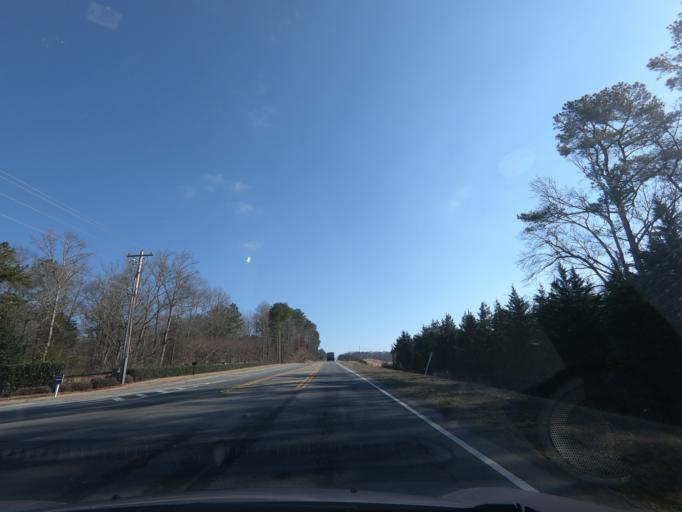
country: US
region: Georgia
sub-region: Forsyth County
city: Cumming
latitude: 34.2998
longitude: -84.2315
